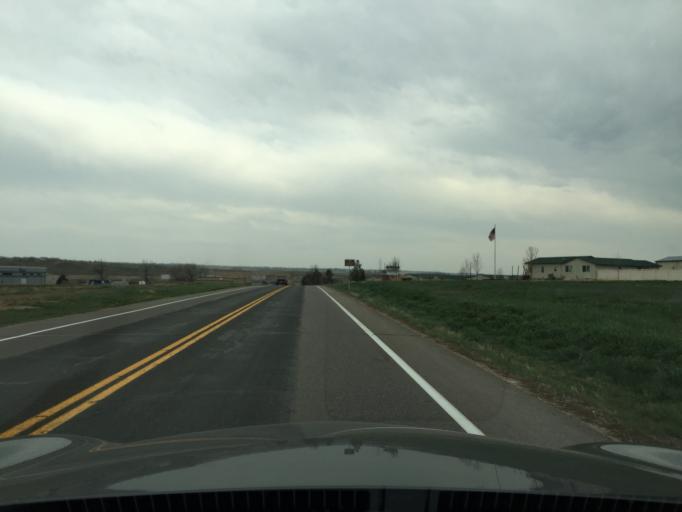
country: US
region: Colorado
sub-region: Boulder County
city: Lafayette
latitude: 40.0108
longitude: -105.0555
